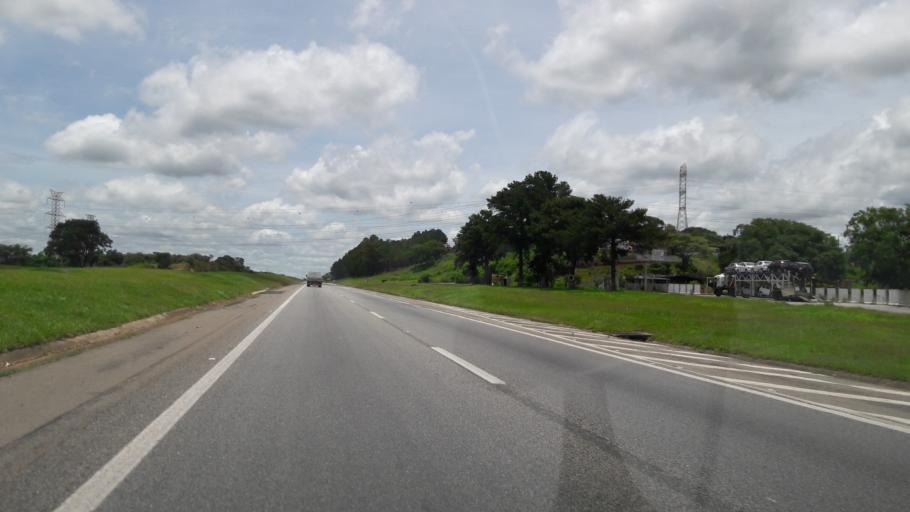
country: BR
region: Sao Paulo
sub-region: Itu
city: Itu
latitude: -23.3875
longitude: -47.3698
